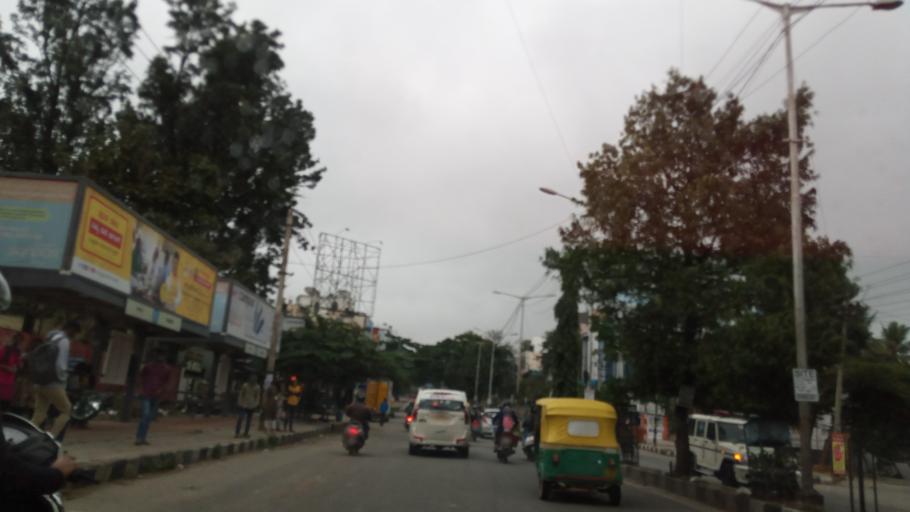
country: IN
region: Karnataka
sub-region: Bangalore Urban
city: Bangalore
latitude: 12.9238
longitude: 77.5539
